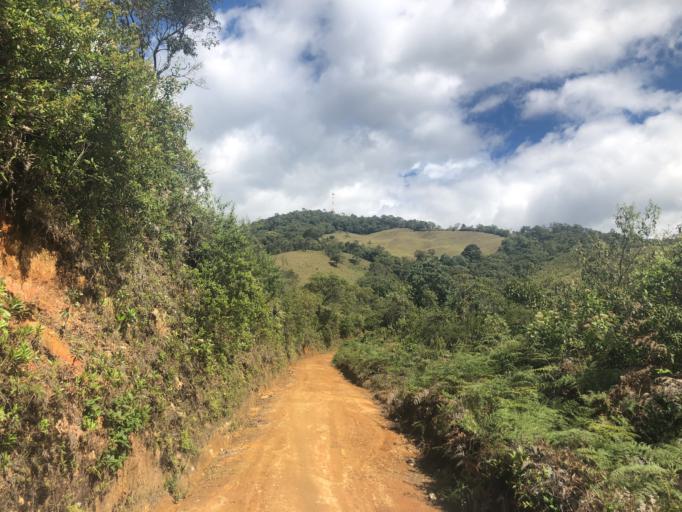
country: CO
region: Cauca
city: Silvia
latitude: 2.6798
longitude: -76.4397
